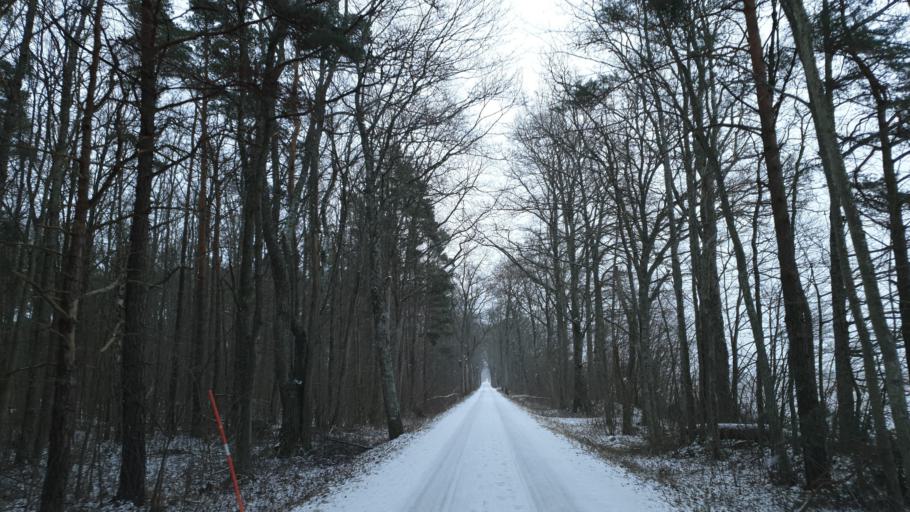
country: SE
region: Gotland
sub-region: Gotland
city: Visby
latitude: 57.5230
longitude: 18.4495
